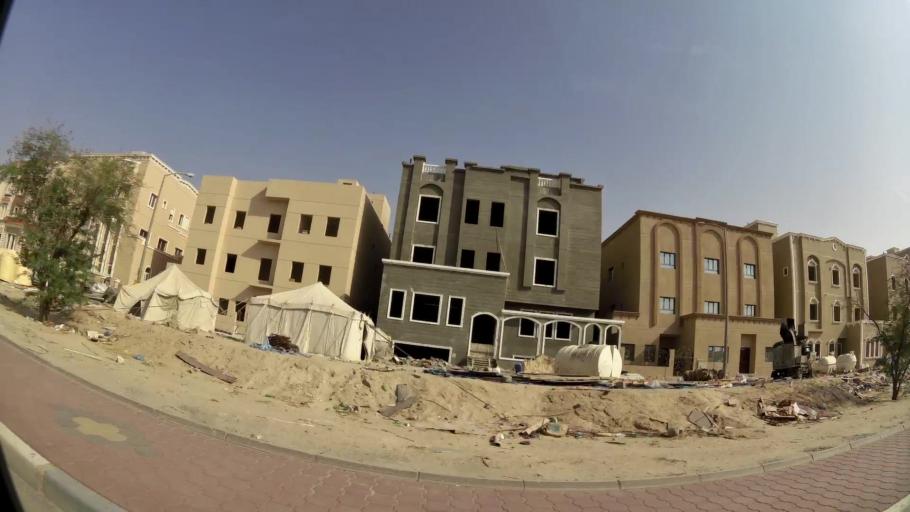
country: KW
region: Muhafazat al Jahra'
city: Al Jahra'
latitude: 29.3221
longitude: 47.6797
